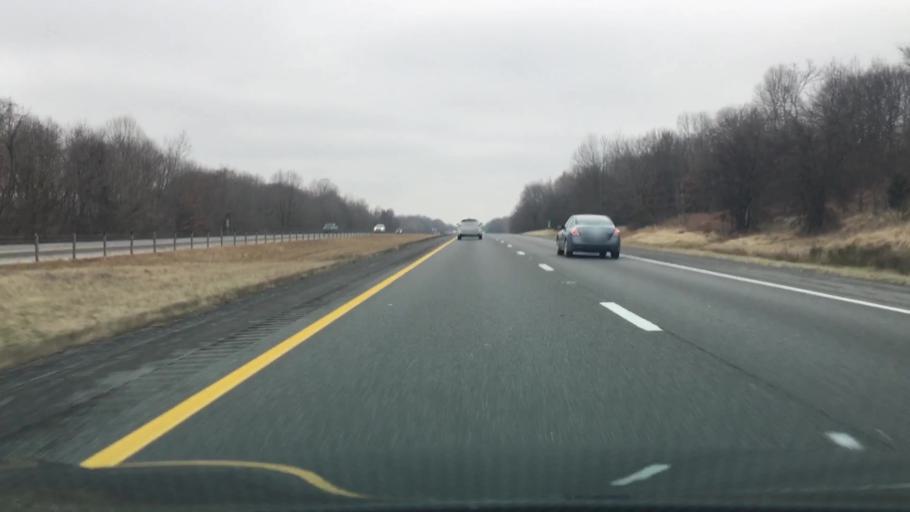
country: US
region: Kentucky
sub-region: McCracken County
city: Reidland
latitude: 36.9981
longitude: -88.5423
